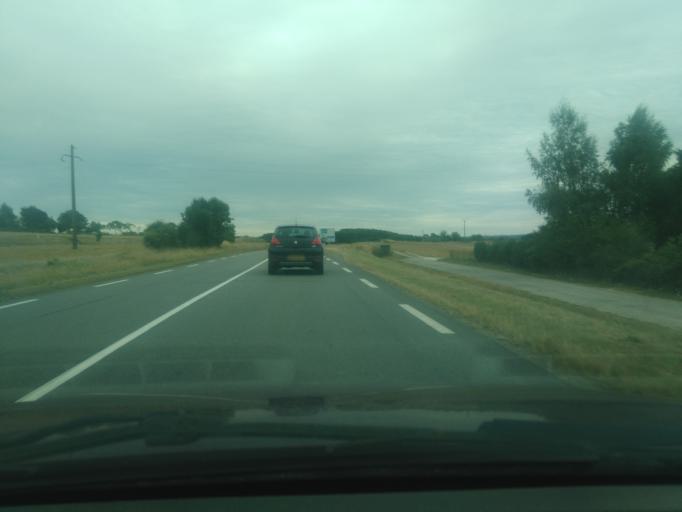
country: FR
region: Centre
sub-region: Departement de l'Indre
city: Saint-Gaultier
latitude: 46.6403
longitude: 1.4316
